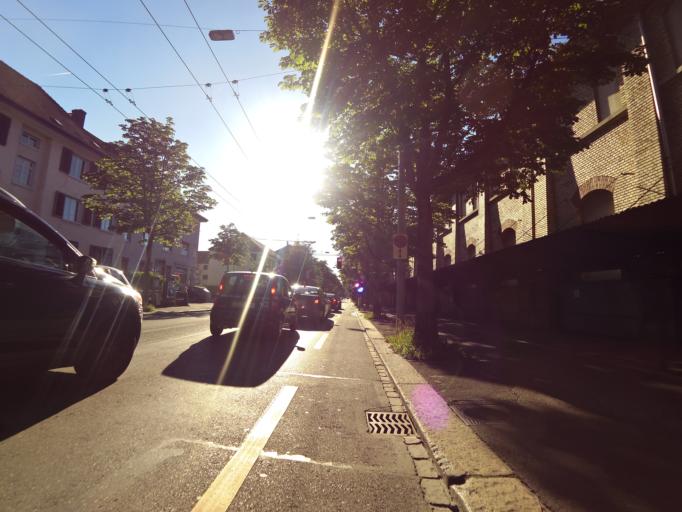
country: CH
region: Zurich
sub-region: Bezirk Zuerich
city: Zuerich (Kreis 4) / Hard
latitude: 47.3867
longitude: 8.5031
